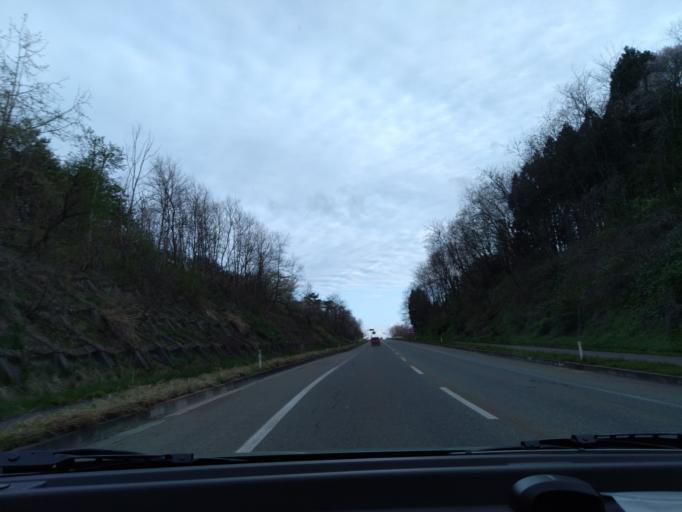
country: JP
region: Akita
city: Akita
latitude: 39.7413
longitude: 140.1369
